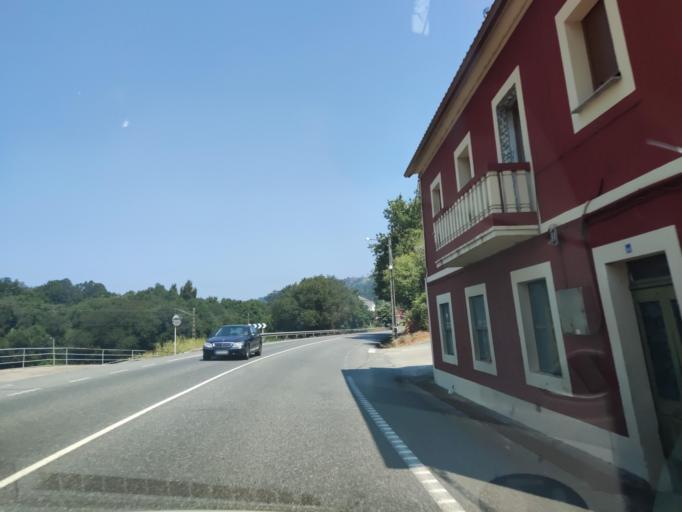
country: ES
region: Galicia
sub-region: Provincia de Pontevedra
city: Redondela
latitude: 42.2237
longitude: -8.5972
